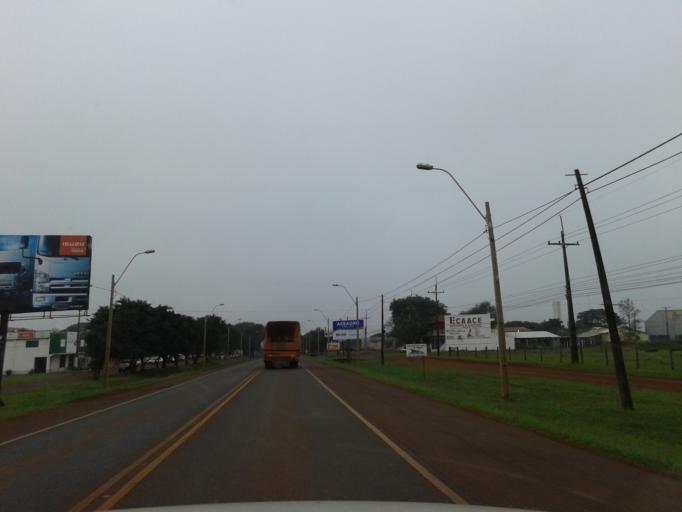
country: PY
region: Alto Parana
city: Santa Rita
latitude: -25.8180
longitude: -55.1100
